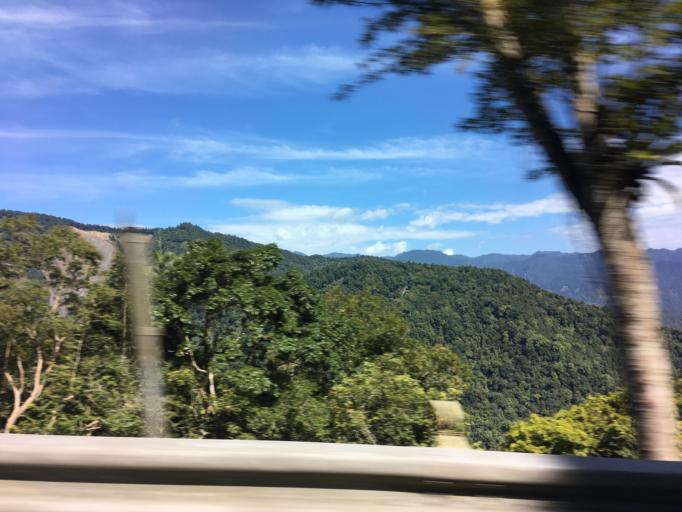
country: TW
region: Taiwan
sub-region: Yilan
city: Yilan
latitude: 24.5411
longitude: 121.5102
